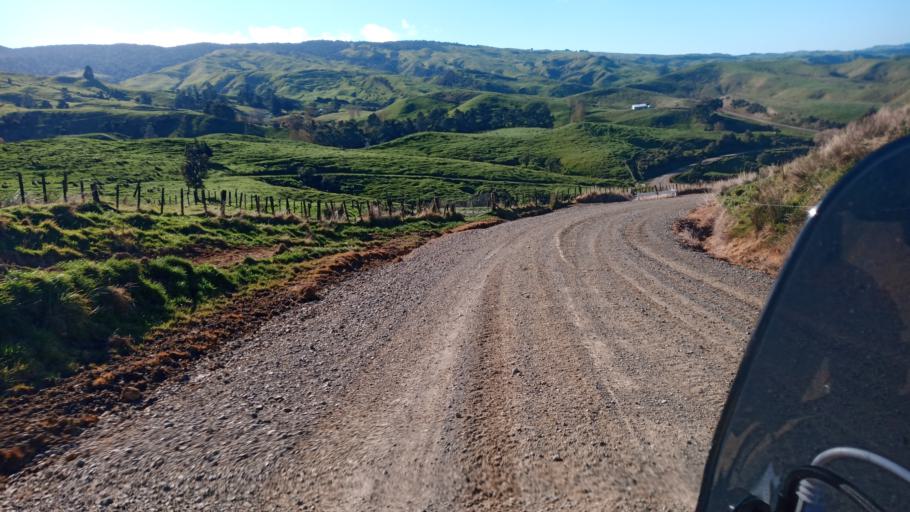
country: NZ
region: Hawke's Bay
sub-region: Wairoa District
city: Wairoa
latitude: -38.7399
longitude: 177.2838
